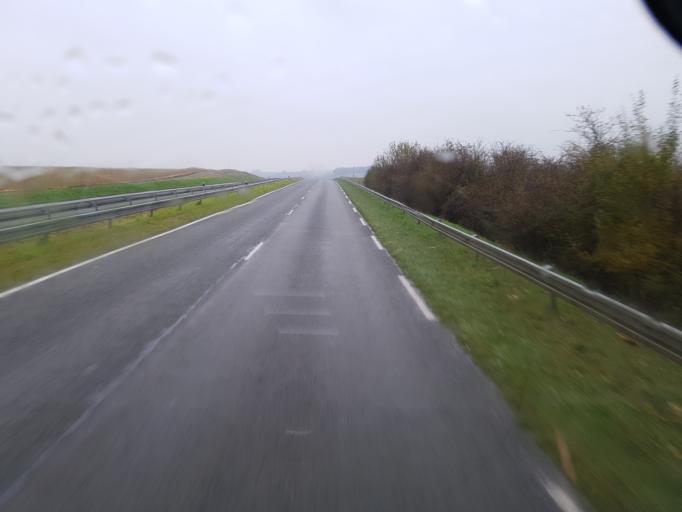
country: FR
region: Picardie
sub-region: Departement de l'Aisne
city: Essigny-le-Grand
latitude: 49.8021
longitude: 3.2857
